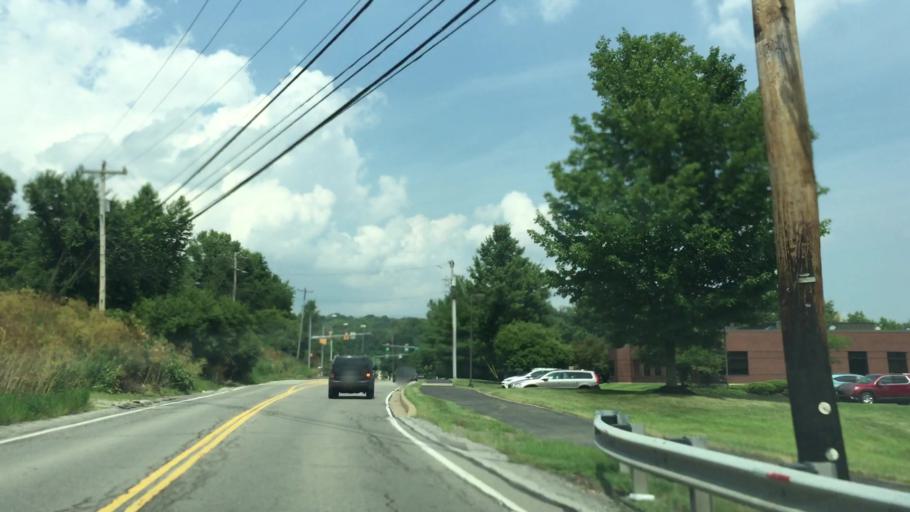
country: US
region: Pennsylvania
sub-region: Allegheny County
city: Enlow
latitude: 40.4553
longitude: -80.1945
